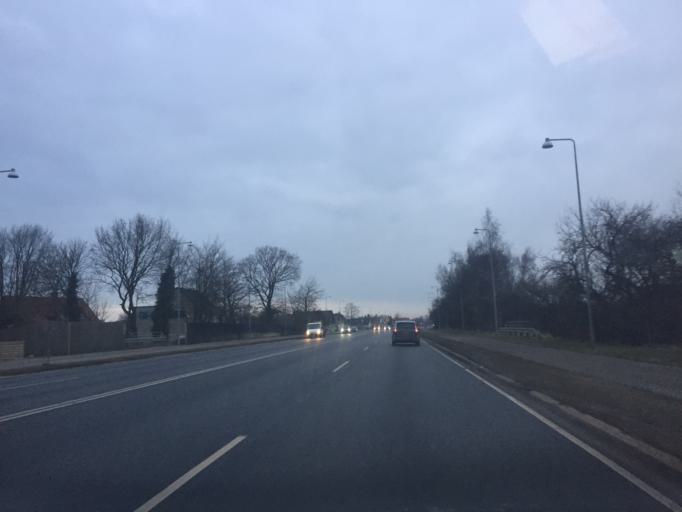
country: DK
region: Zealand
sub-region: Koge Kommune
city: Koge
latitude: 55.4947
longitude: 12.1926
